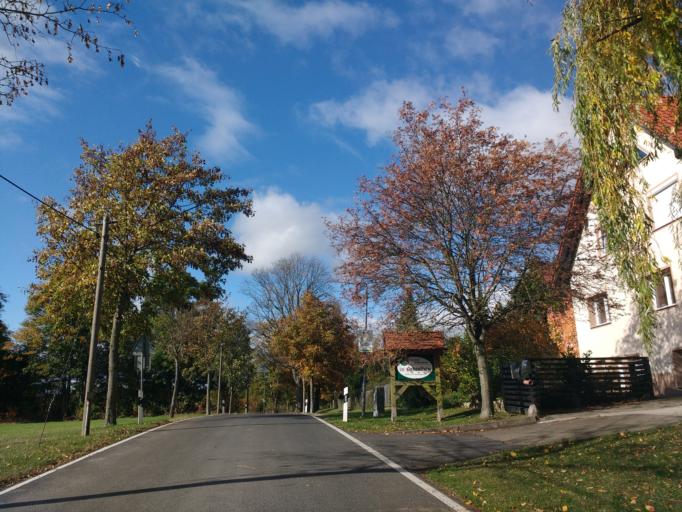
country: DE
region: Thuringia
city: Worbis
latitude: 51.4520
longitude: 10.3491
